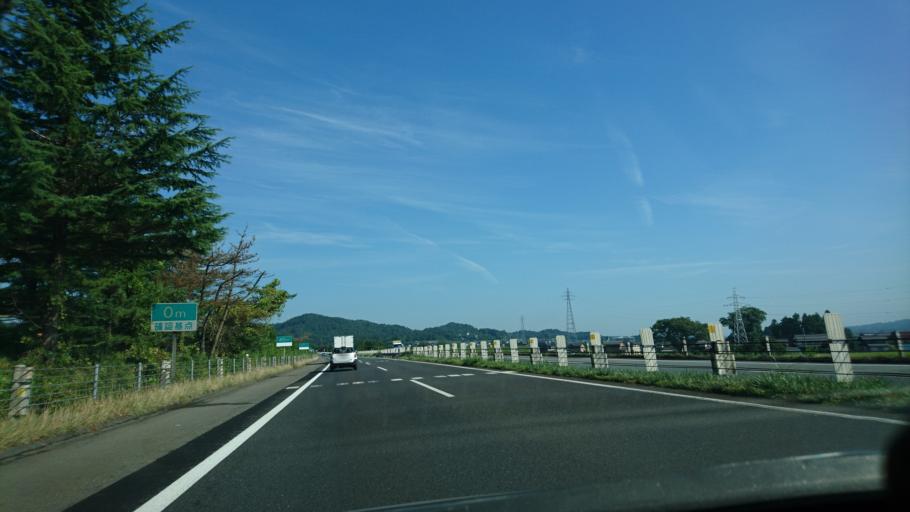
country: JP
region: Iwate
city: Ichinoseki
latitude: 38.9761
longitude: 141.1111
